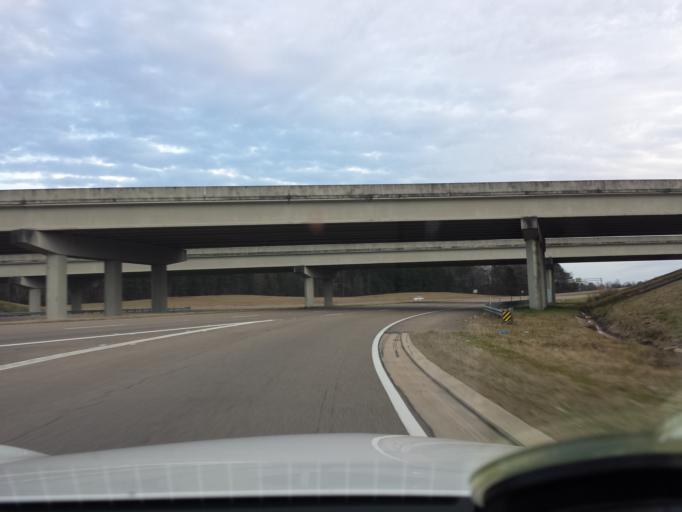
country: US
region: Mississippi
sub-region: Winston County
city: Louisville
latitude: 33.1575
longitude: -89.0878
